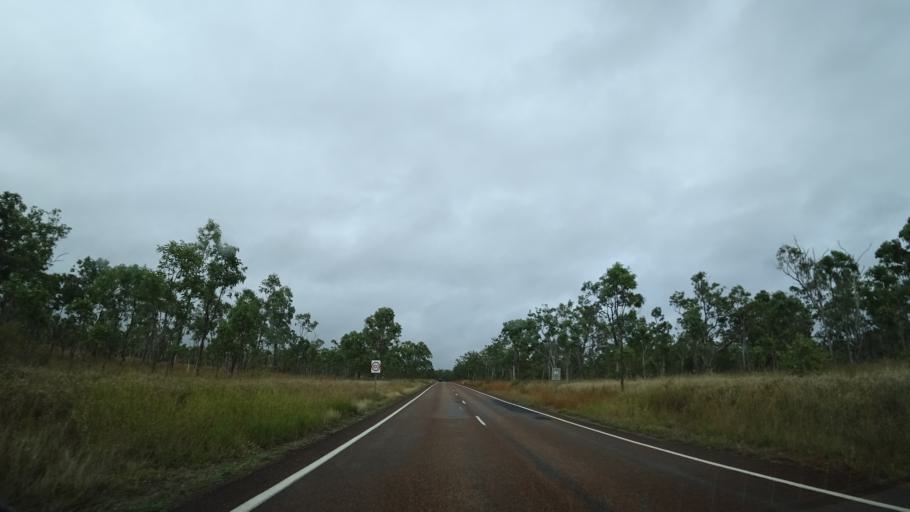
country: AU
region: Queensland
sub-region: Tablelands
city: Ravenshoe
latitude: -17.6736
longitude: 145.2371
